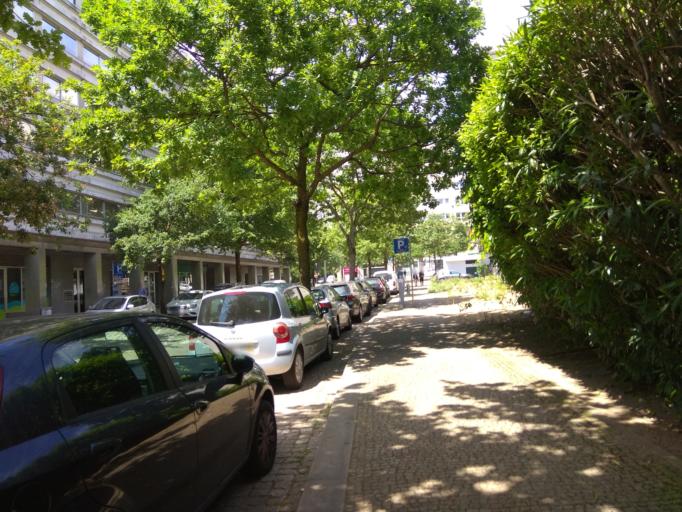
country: PT
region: Porto
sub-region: Maia
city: Maia
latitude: 41.2318
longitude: -8.6244
